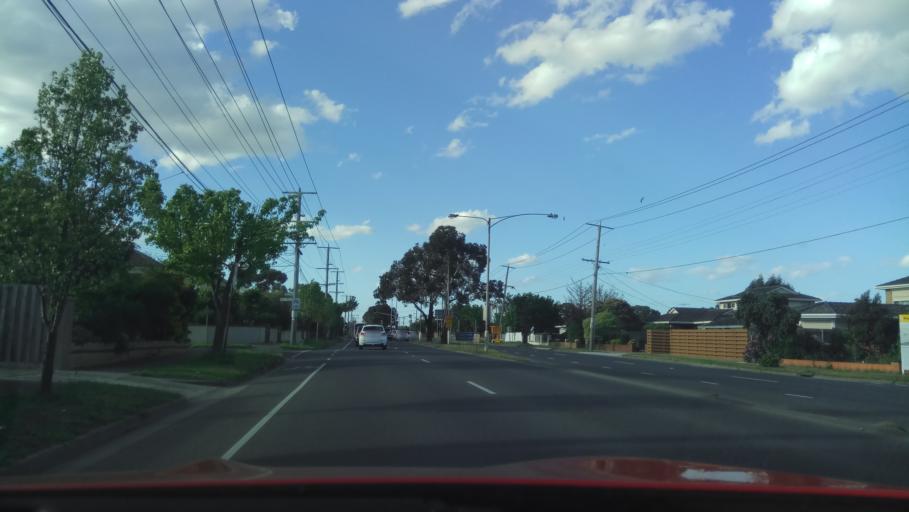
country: AU
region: Victoria
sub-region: Hobsons Bay
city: Altona North
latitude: -37.8402
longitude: 144.8466
